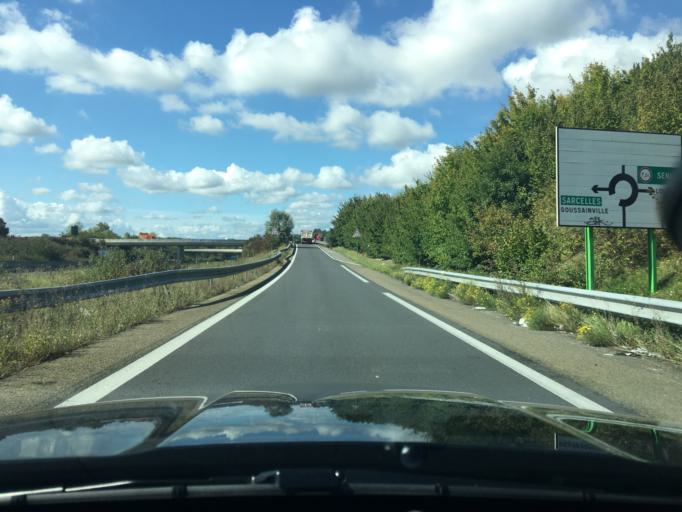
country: FR
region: Ile-de-France
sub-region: Departement du Val-d'Oise
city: Louvres
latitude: 49.0288
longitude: 2.5035
